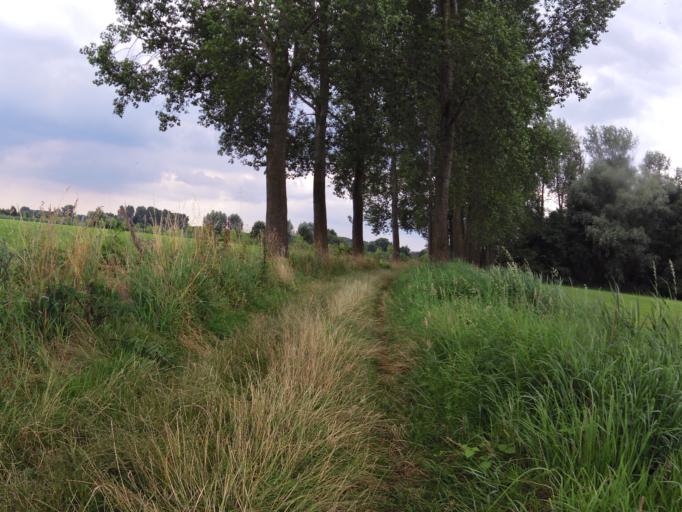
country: NL
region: North Brabant
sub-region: Gemeente Schijndel
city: Schijndel
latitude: 51.5845
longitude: 5.3900
